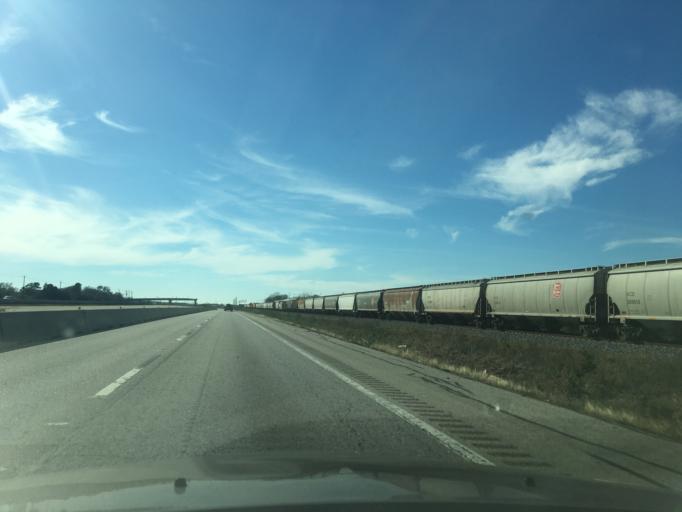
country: US
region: Texas
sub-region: Wharton County
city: East Bernard
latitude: 29.4721
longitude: -95.9596
